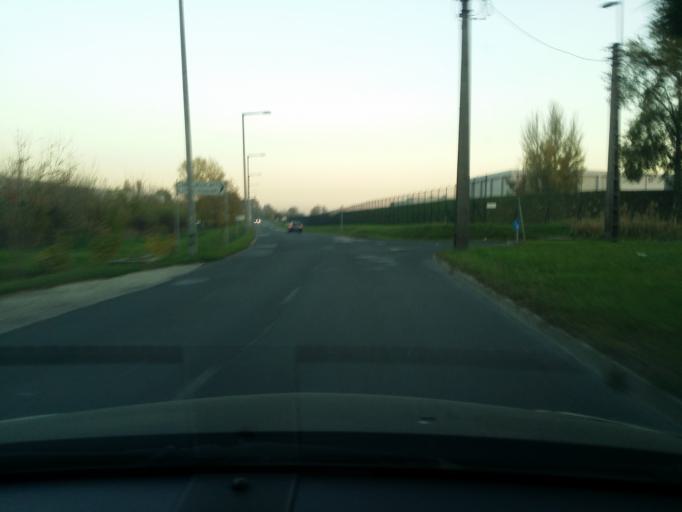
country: HU
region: Budapest
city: Budapest XV. keruelet
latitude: 47.5832
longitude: 19.1354
